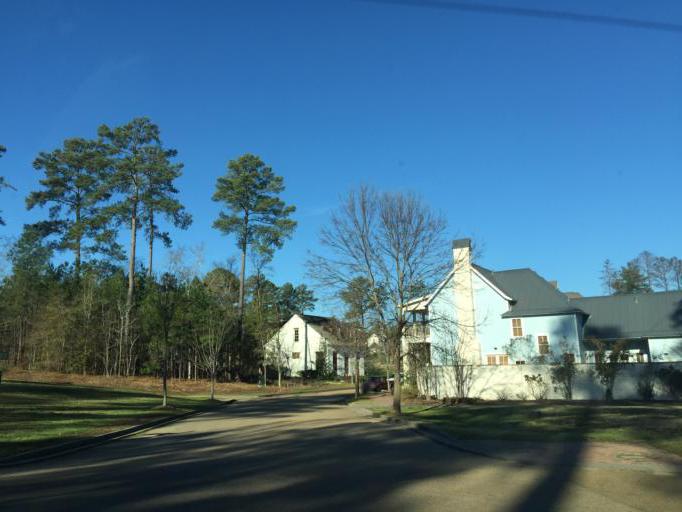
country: US
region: Mississippi
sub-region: Madison County
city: Madison
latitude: 32.4592
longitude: -90.0559
